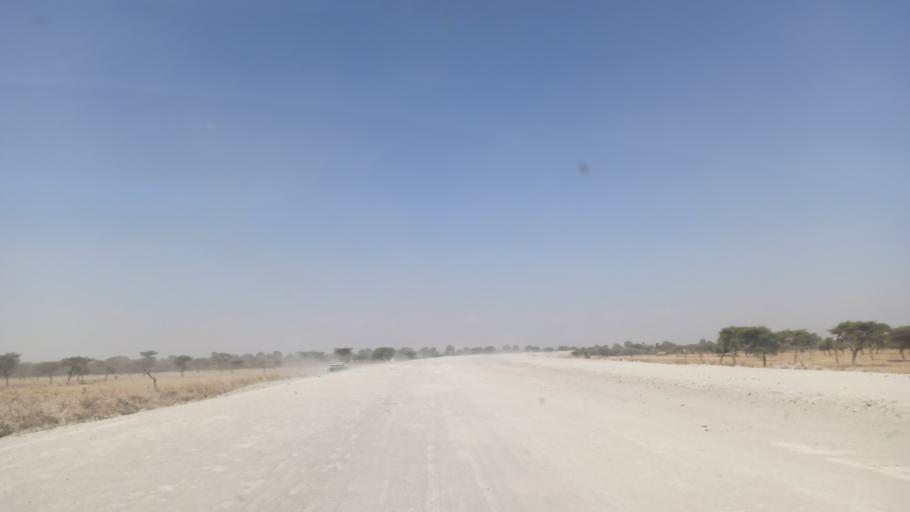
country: ET
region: Oromiya
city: Ziway
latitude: 7.6947
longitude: 38.6482
